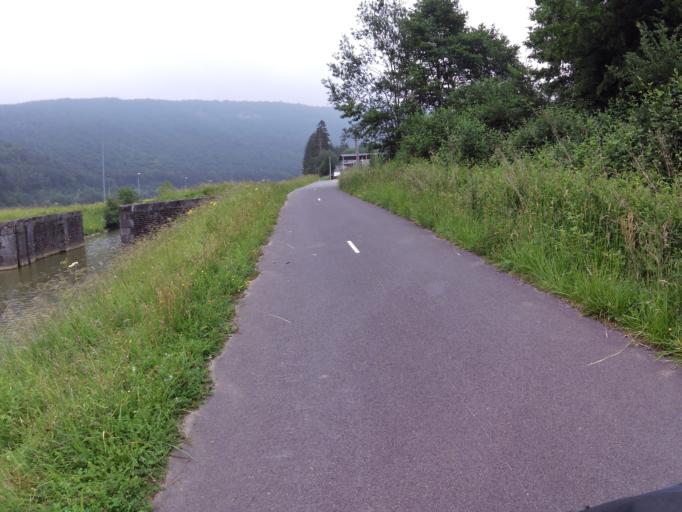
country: FR
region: Champagne-Ardenne
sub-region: Departement des Ardennes
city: Haybes
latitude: 50.0016
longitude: 4.6955
